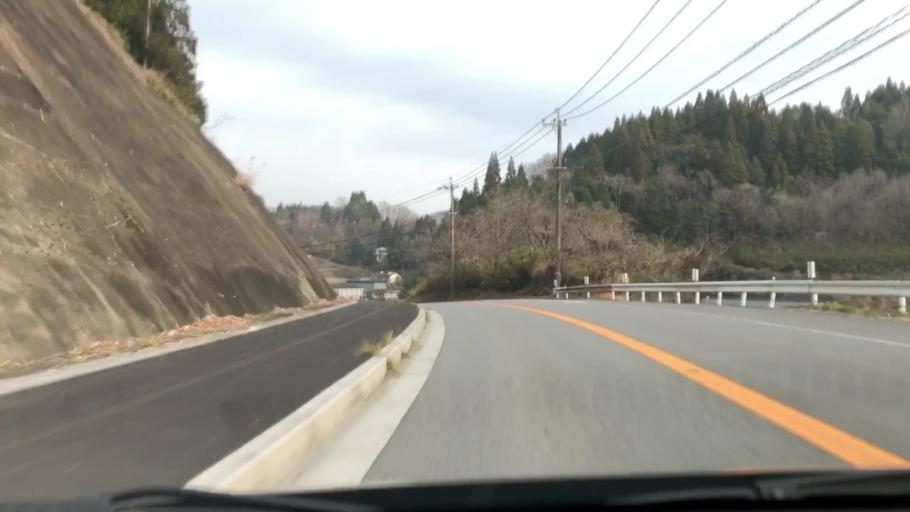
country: JP
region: Oita
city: Takedamachi
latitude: 32.9755
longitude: 131.5293
